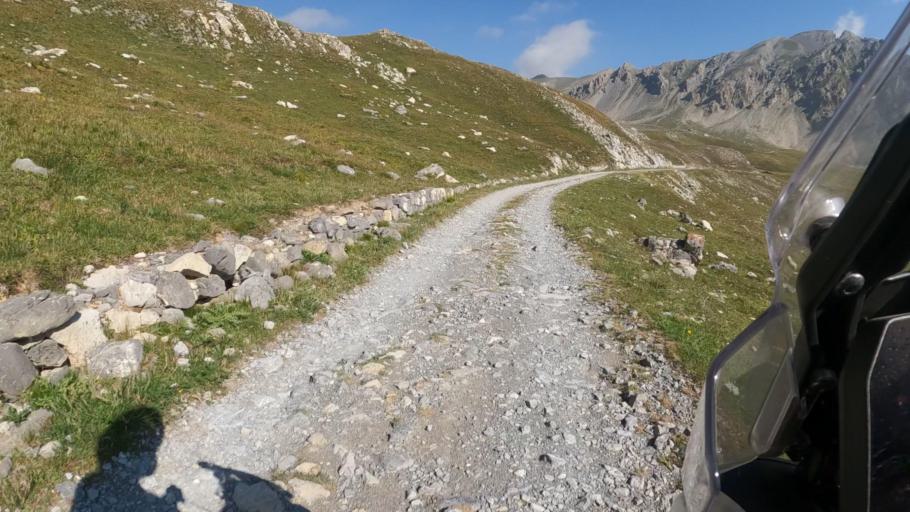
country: IT
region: Piedmont
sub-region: Provincia di Cuneo
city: Bersezio
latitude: 44.4012
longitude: 7.0162
